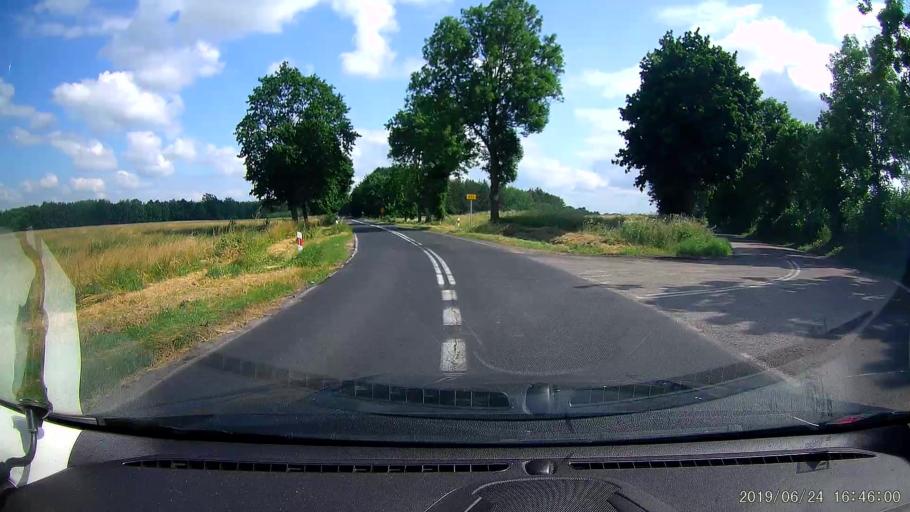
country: PL
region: Lublin Voivodeship
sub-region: Powiat tomaszowski
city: Laszczow
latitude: 50.5300
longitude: 23.6726
